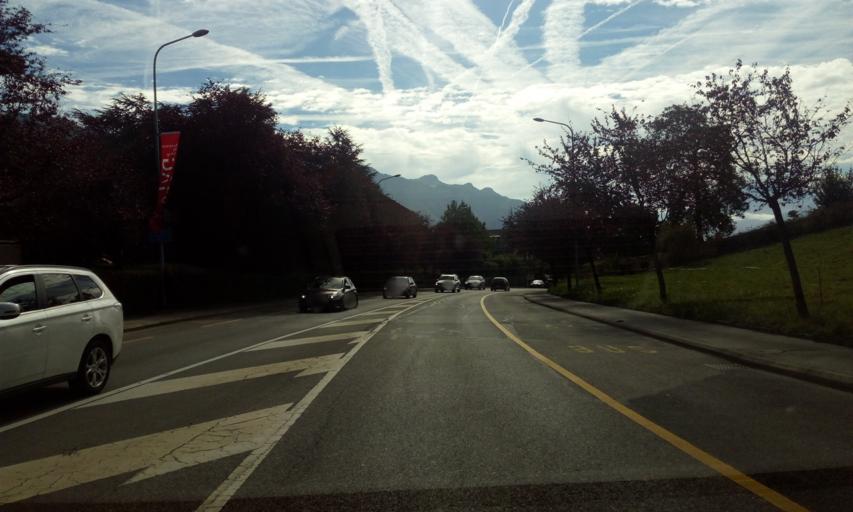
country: CH
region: Vaud
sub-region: Riviera-Pays-d'Enhaut District
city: Le Chatelard
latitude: 46.4497
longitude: 6.8912
